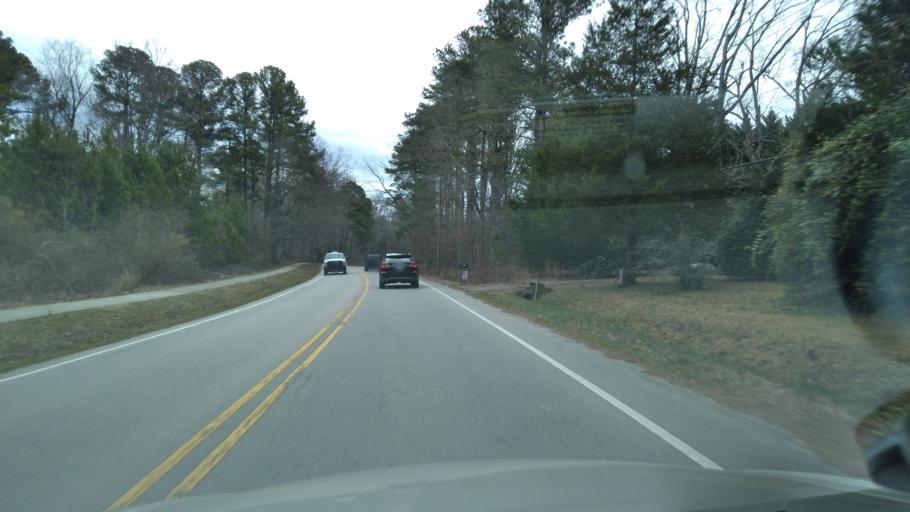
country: US
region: North Carolina
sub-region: Wake County
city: Apex
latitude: 35.7343
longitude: -78.8378
